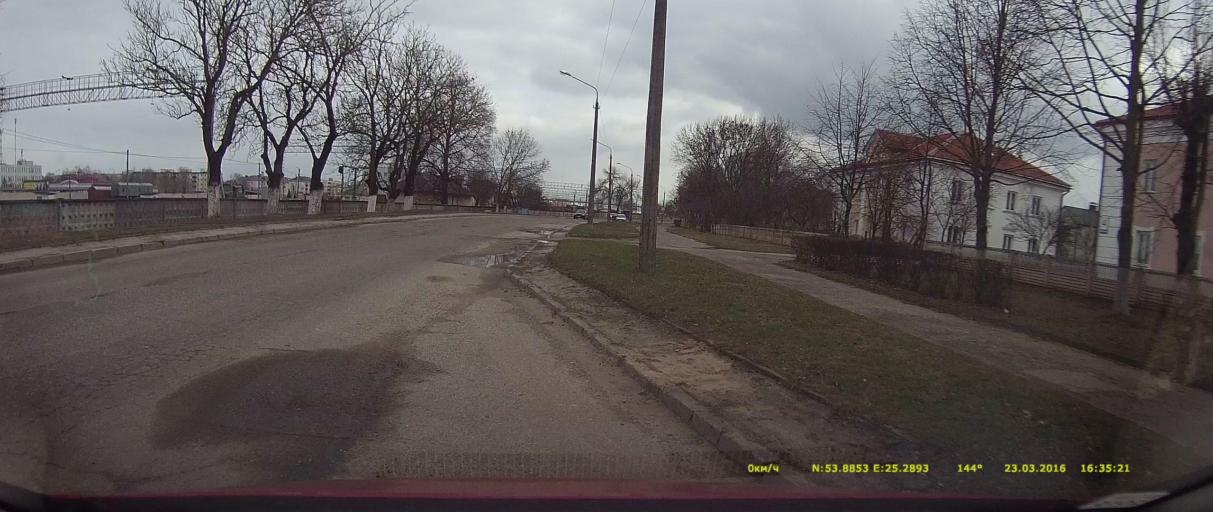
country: BY
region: Grodnenskaya
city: Lida
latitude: 53.8853
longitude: 25.2893
